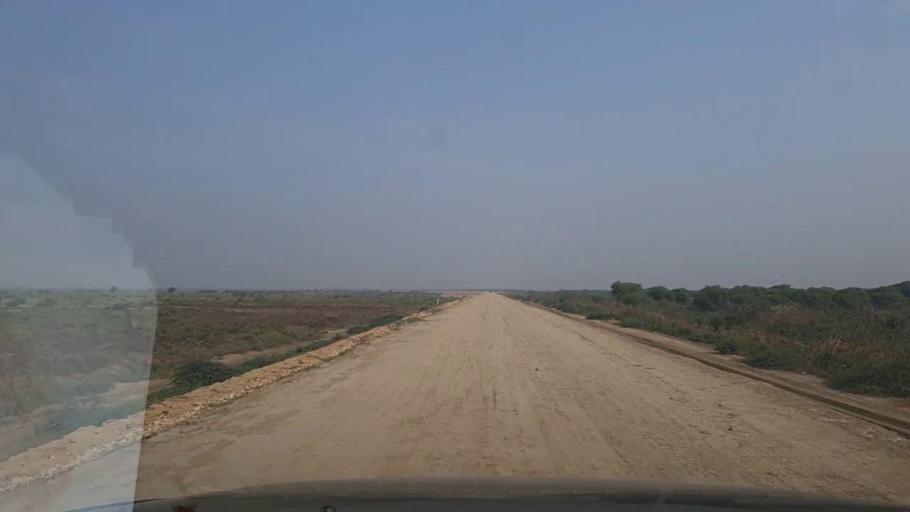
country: PK
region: Sindh
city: Bulri
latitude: 24.9498
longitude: 68.2899
